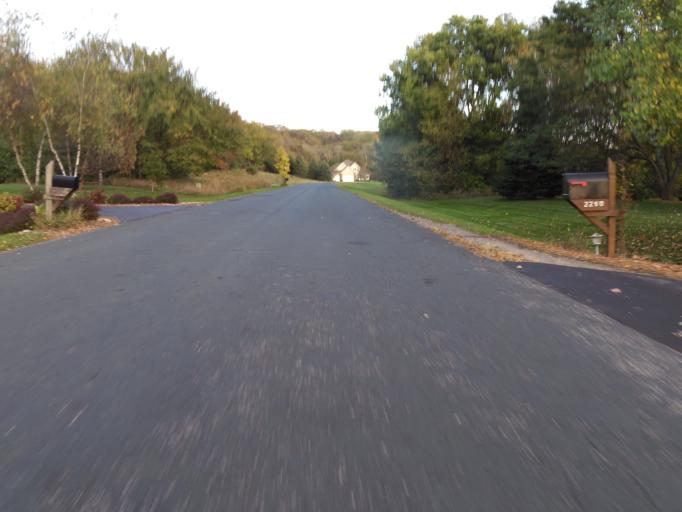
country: US
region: Minnesota
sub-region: Washington County
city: Bayport
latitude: 44.9827
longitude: -92.8077
